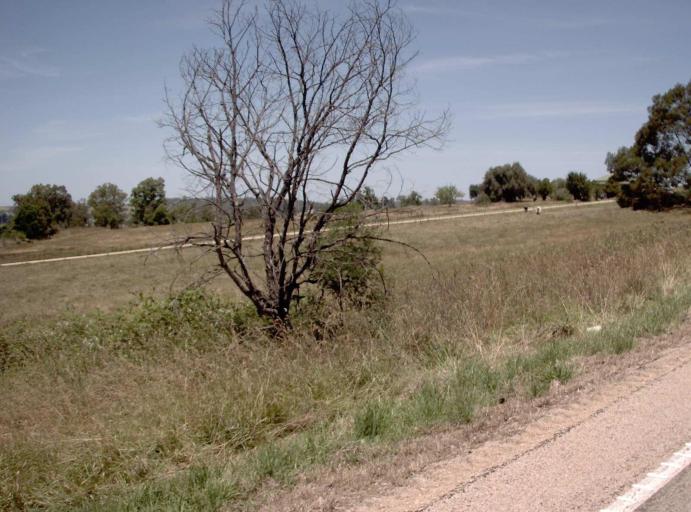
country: AU
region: Victoria
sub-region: East Gippsland
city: Bairnsdale
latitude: -37.7212
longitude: 147.8043
